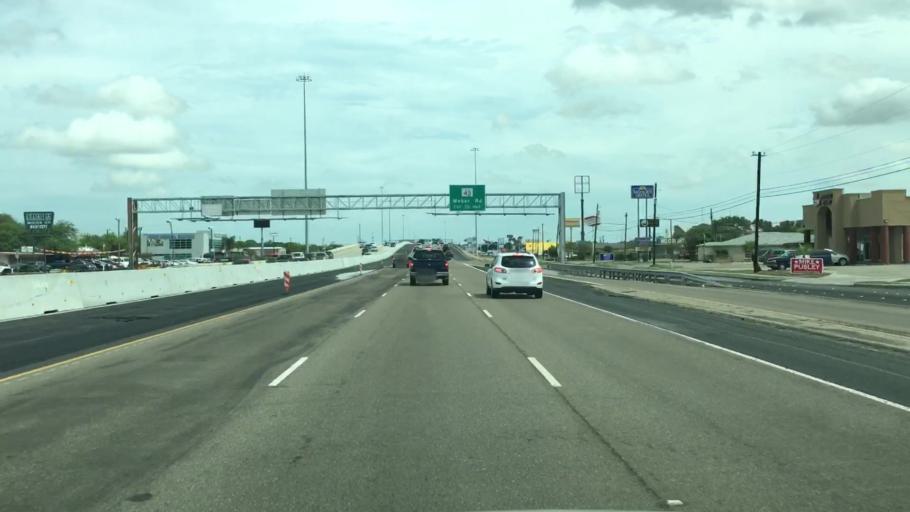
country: US
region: Texas
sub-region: Nueces County
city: Corpus Christi
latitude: 27.7269
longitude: -97.4097
